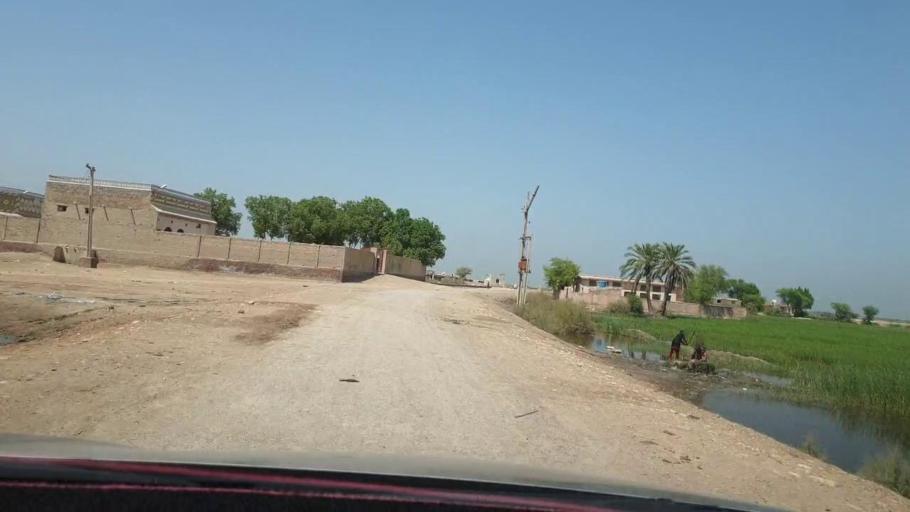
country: PK
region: Sindh
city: Warah
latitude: 27.5782
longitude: 67.7581
